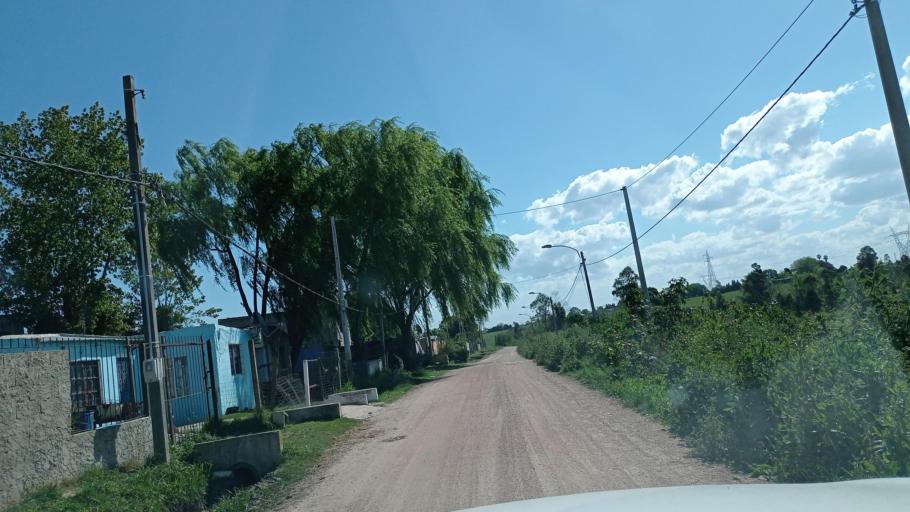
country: UY
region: Canelones
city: La Paz
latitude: -34.7805
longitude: -56.1578
